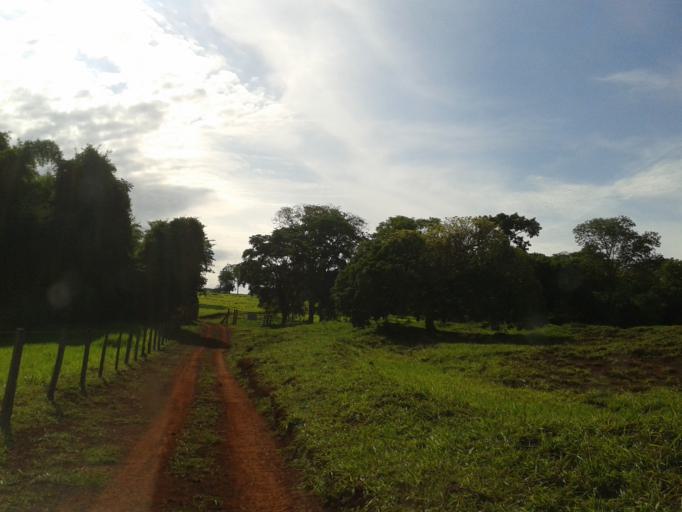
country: BR
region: Minas Gerais
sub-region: Centralina
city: Centralina
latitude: -18.7077
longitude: -49.1973
